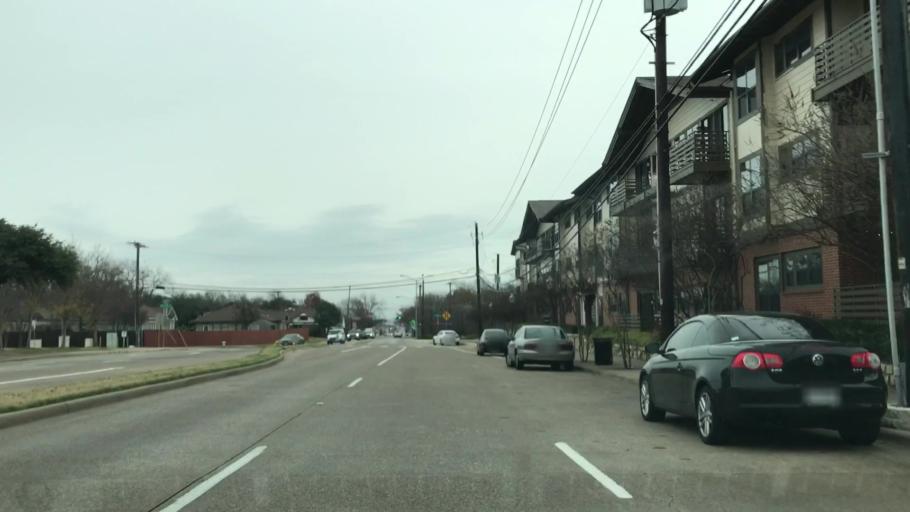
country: US
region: Texas
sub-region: Dallas County
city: Cockrell Hill
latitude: 32.7495
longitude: -96.8491
